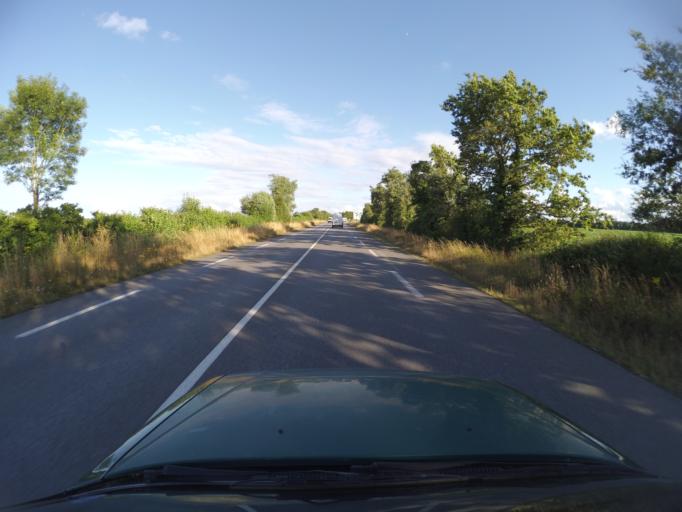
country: FR
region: Pays de la Loire
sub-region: Departement de la Vendee
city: Saint-Hilaire-de-Loulay
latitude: 47.0124
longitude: -1.3396
